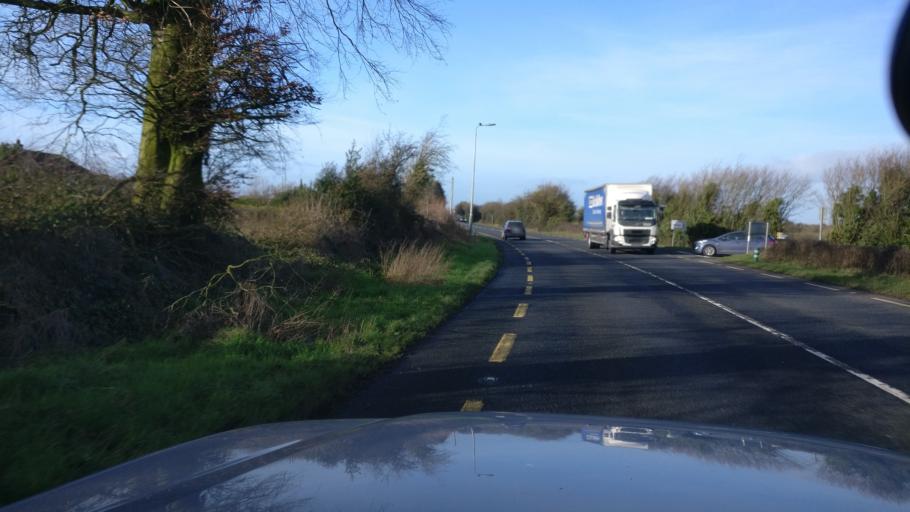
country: IE
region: Leinster
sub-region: Uibh Fhaili
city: Tullamore
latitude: 53.2054
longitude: -7.4343
